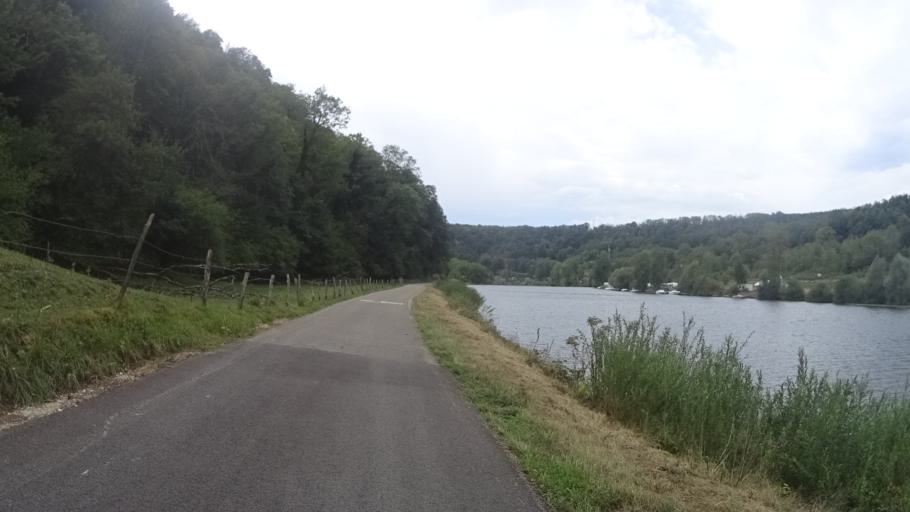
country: FR
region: Franche-Comte
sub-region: Departement du Doubs
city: Baume-les-Dames
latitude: 47.3521
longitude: 6.3831
